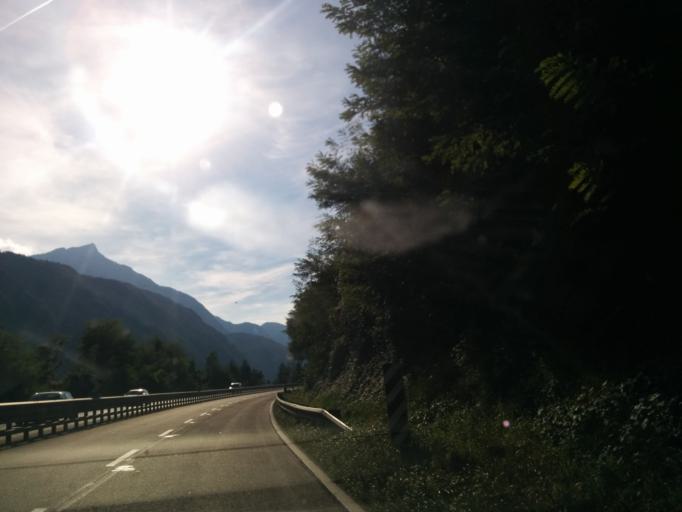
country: IT
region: Trentino-Alto Adige
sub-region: Provincia di Trento
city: Novaledo
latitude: 46.0228
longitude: 11.3706
